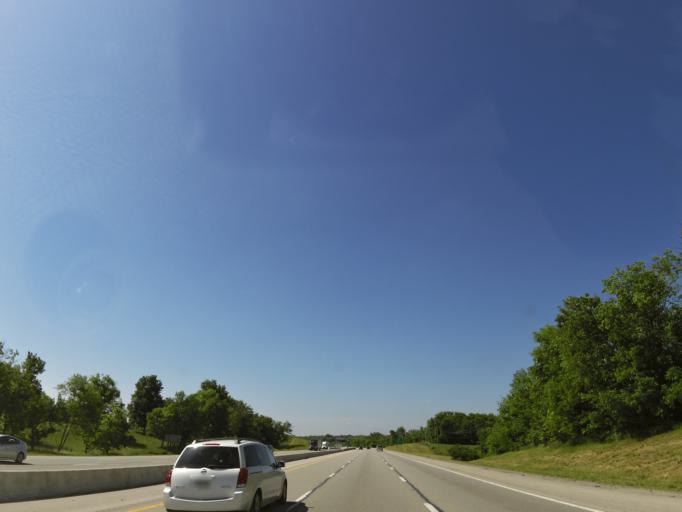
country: US
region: Kentucky
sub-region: Madison County
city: Berea
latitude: 37.6331
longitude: -84.3165
